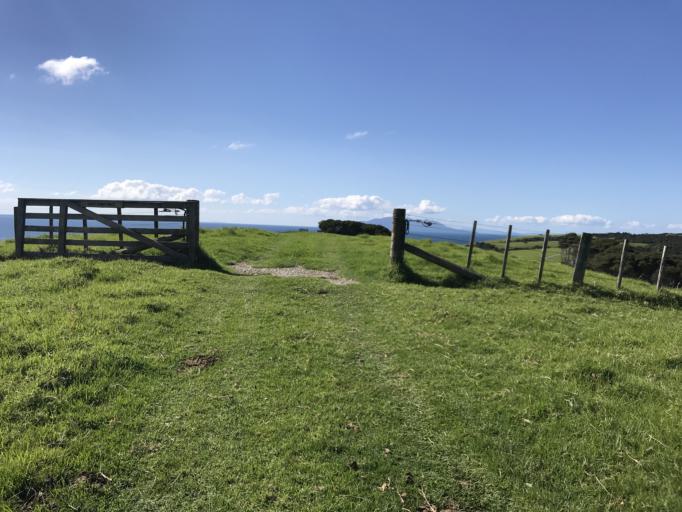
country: NZ
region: Auckland
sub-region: Auckland
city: Warkworth
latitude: -36.3747
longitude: 174.8329
